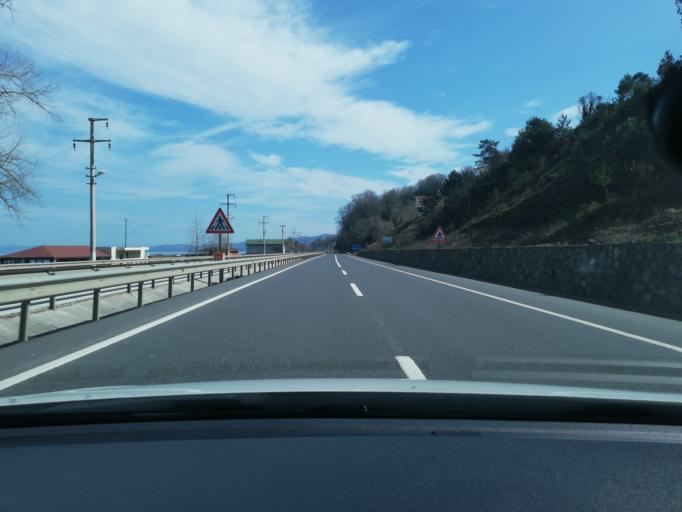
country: TR
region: Duzce
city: Akcakoca
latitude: 41.0958
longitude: 31.2027
